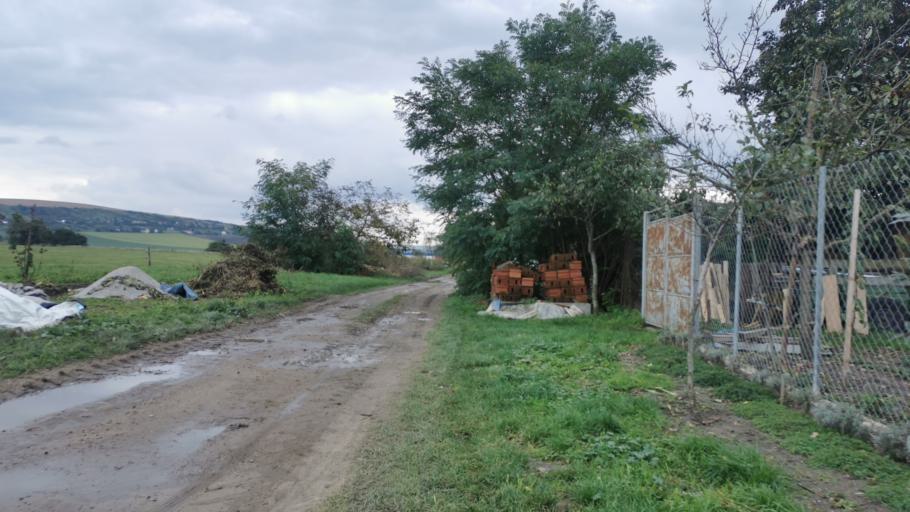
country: SK
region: Trnavsky
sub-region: Okres Skalica
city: Holic
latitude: 48.8222
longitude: 17.1942
